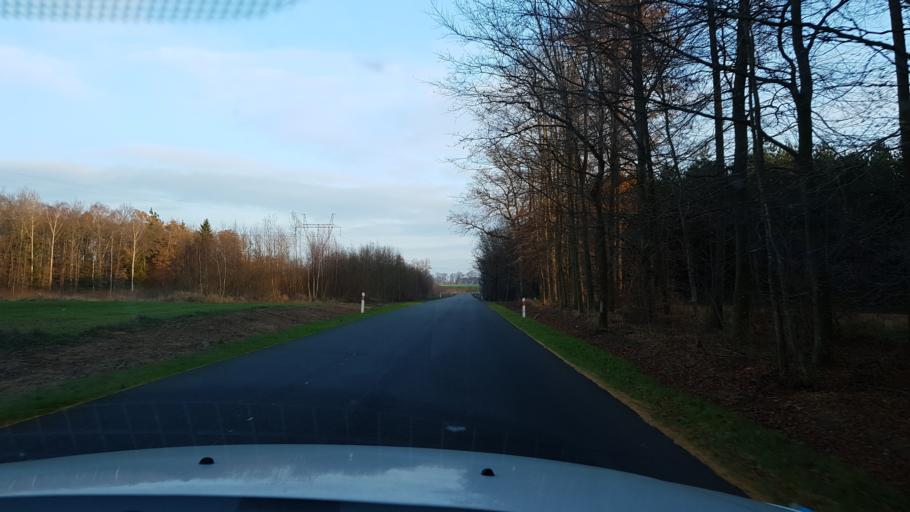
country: PL
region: West Pomeranian Voivodeship
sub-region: Koszalin
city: Koszalin
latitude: 54.1196
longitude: 16.1043
